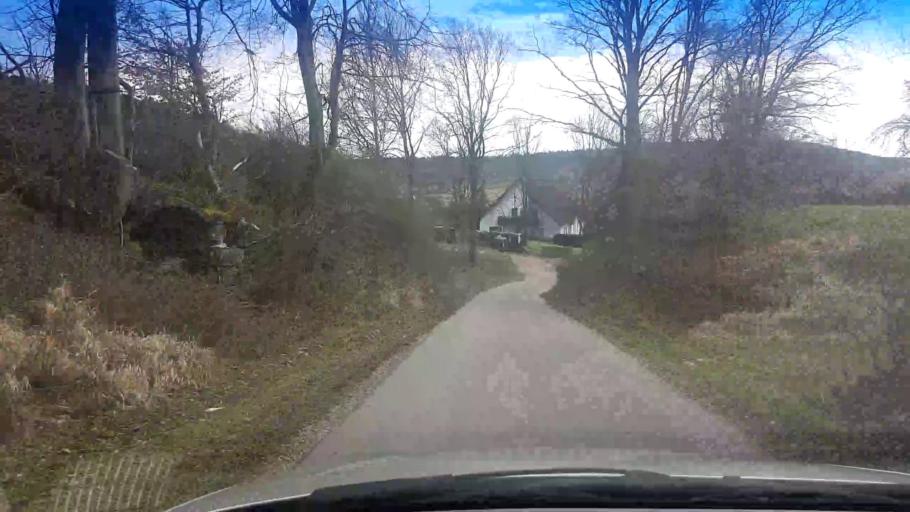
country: DE
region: Bavaria
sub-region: Upper Franconia
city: Burgebrach
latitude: 49.7993
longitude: 10.7662
